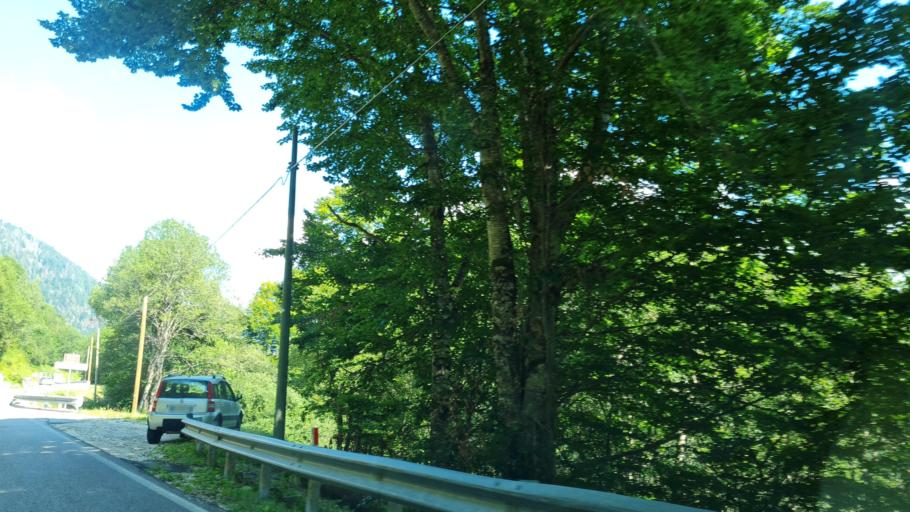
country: IT
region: Trentino-Alto Adige
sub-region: Provincia di Trento
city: Carzano
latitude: 46.1163
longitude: 11.4908
